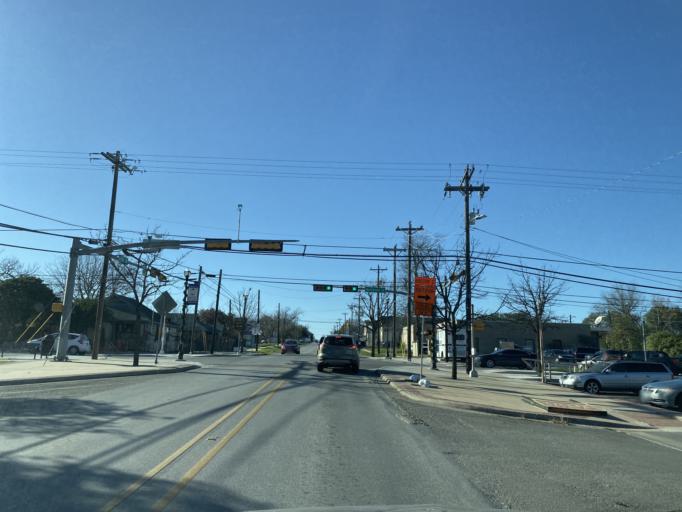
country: US
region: Texas
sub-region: Hays County
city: Kyle
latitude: 29.9888
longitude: -97.8769
